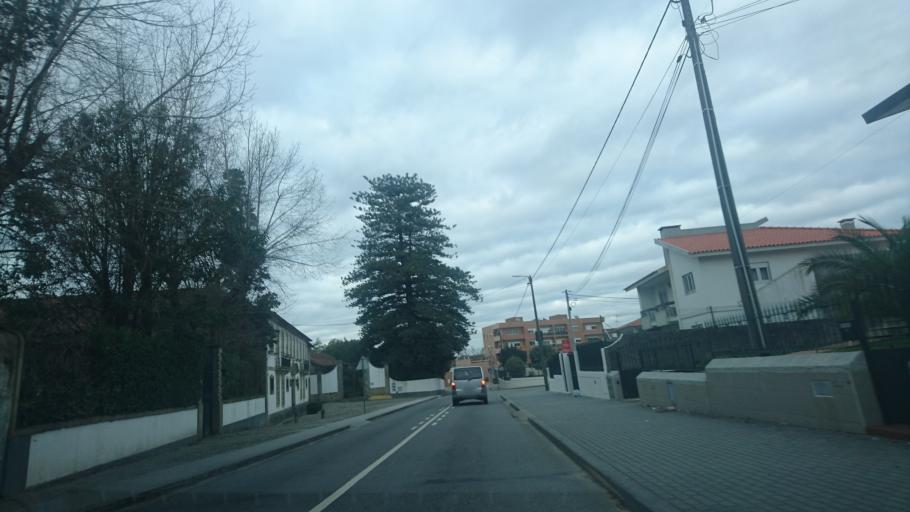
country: PT
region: Aveiro
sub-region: Santa Maria da Feira
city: Pacos de Brandao
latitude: 40.9700
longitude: -8.5910
